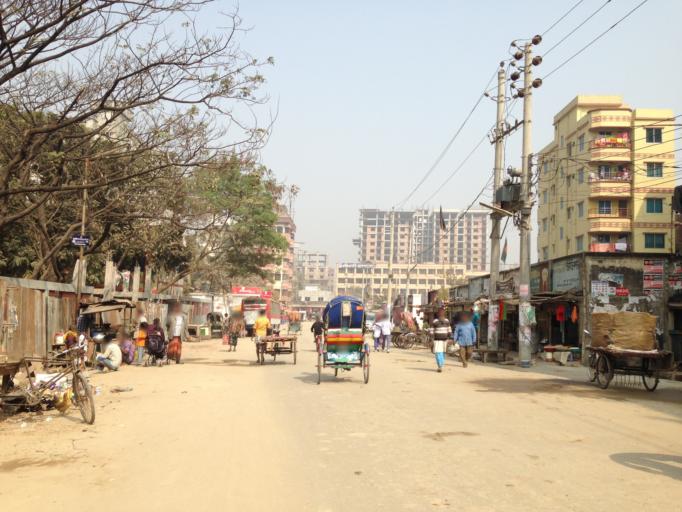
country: BD
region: Dhaka
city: Azimpur
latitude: 23.8065
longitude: 90.3808
